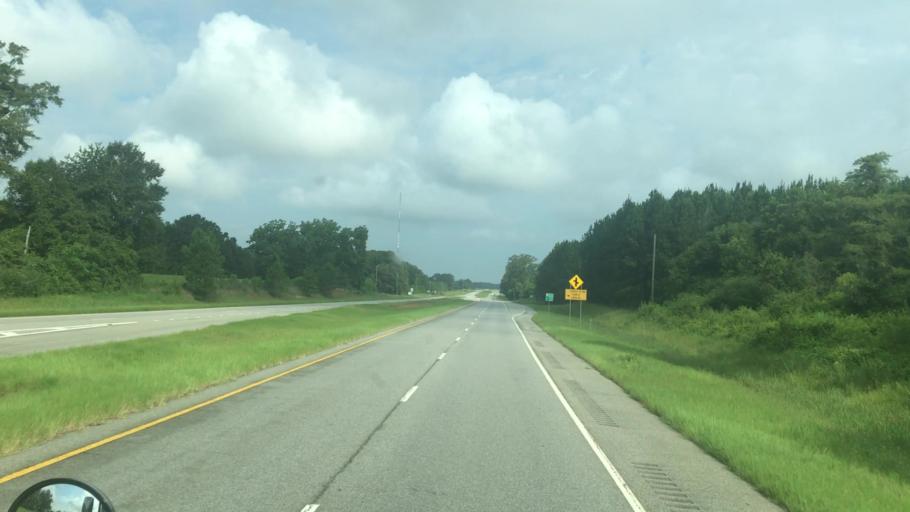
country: US
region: Georgia
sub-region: Miller County
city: Colquitt
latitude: 31.2575
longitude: -84.8081
